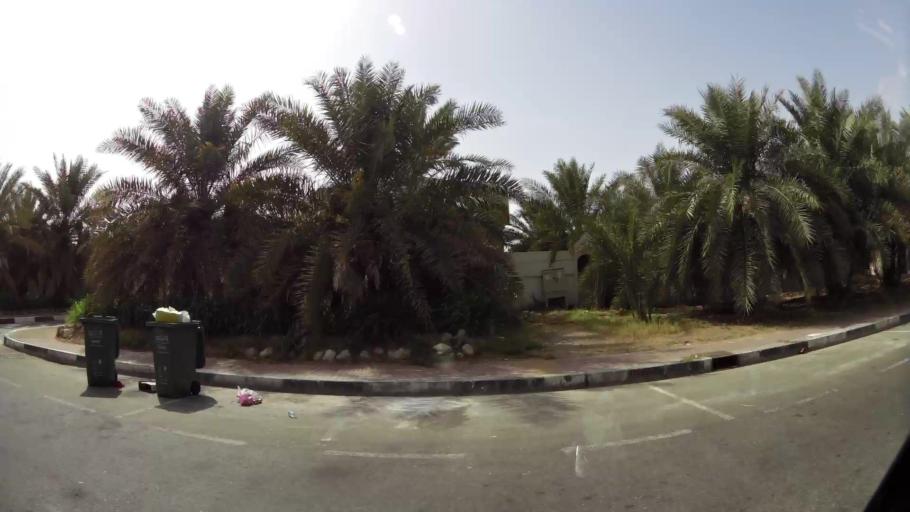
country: AE
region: Abu Dhabi
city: Al Ain
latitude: 24.1616
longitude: 55.6932
